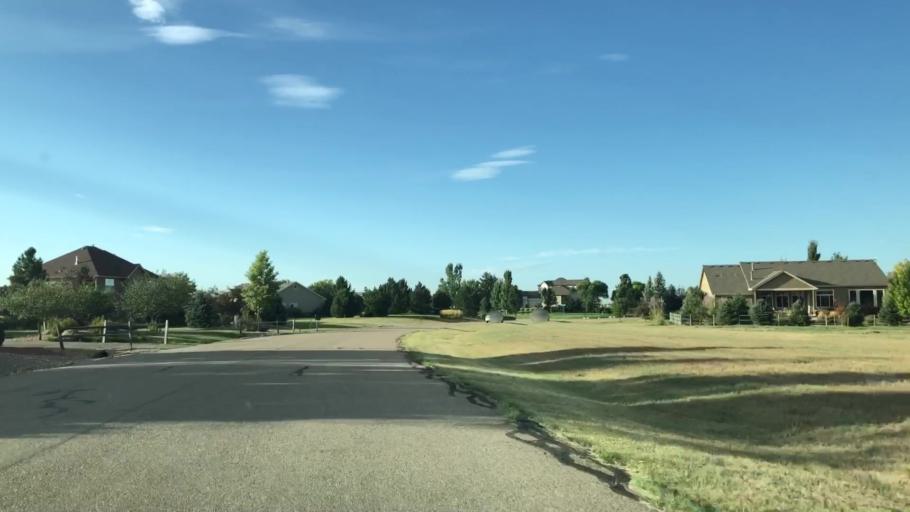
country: US
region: Colorado
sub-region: Weld County
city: Windsor
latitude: 40.4398
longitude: -104.9464
